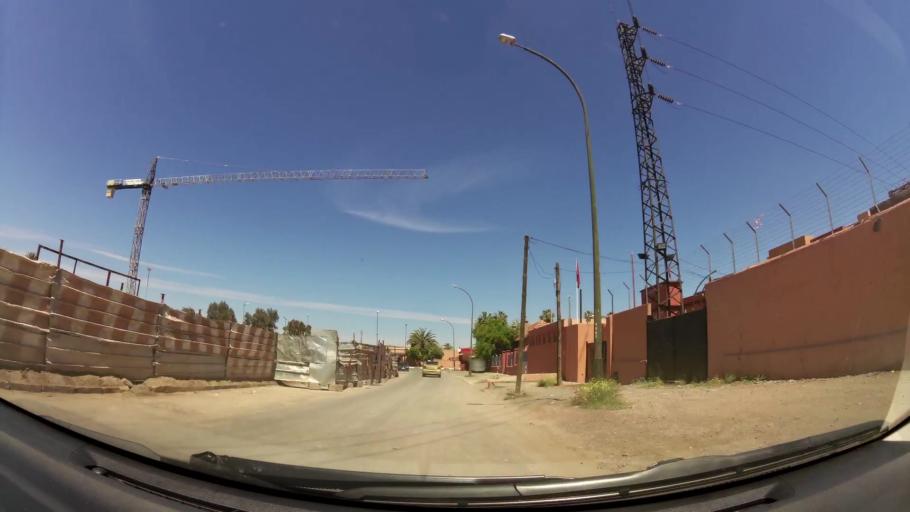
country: MA
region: Marrakech-Tensift-Al Haouz
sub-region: Marrakech
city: Marrakesh
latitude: 31.6282
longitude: -8.0195
